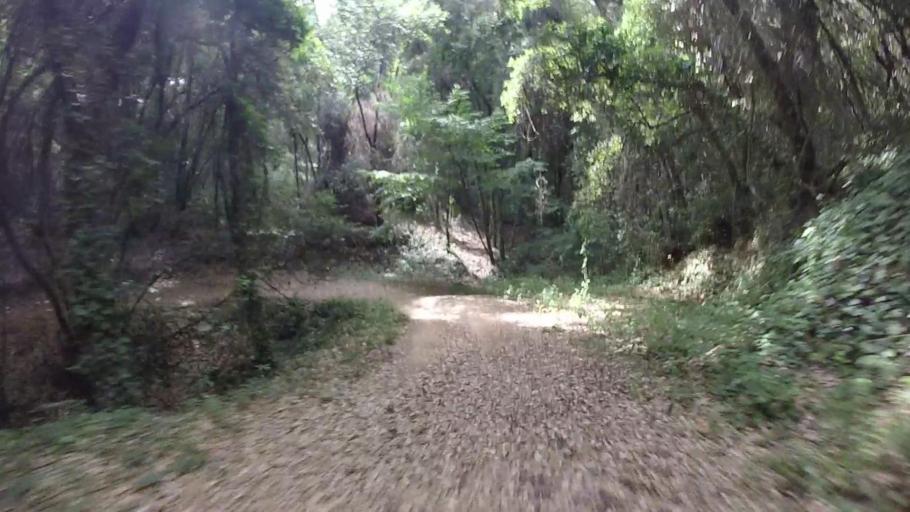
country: FR
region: Provence-Alpes-Cote d'Azur
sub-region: Departement des Alpes-Maritimes
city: Biot
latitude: 43.6149
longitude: 7.0897
